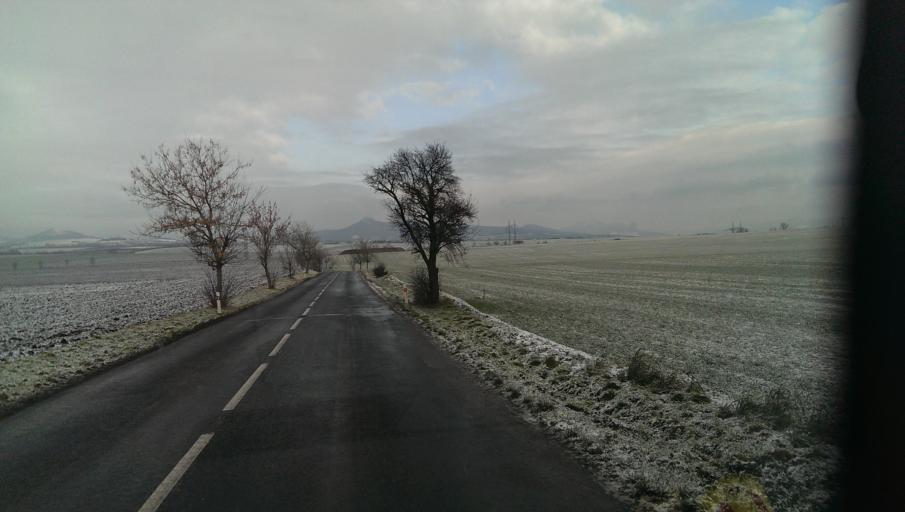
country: CZ
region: Ustecky
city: Trebenice
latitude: 50.4424
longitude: 14.0008
